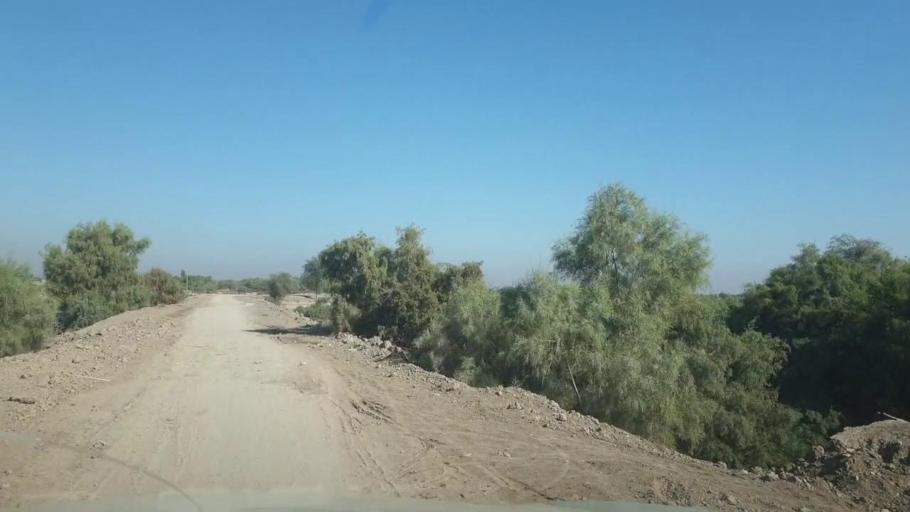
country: PK
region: Sindh
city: Bhan
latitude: 26.5436
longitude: 67.6544
